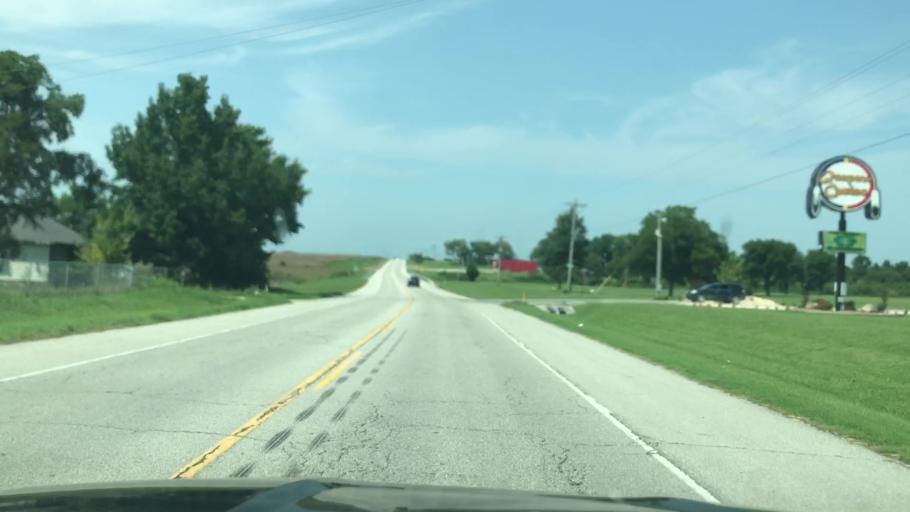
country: US
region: Oklahoma
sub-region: Ottawa County
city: Commerce
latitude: 36.9211
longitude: -94.8419
